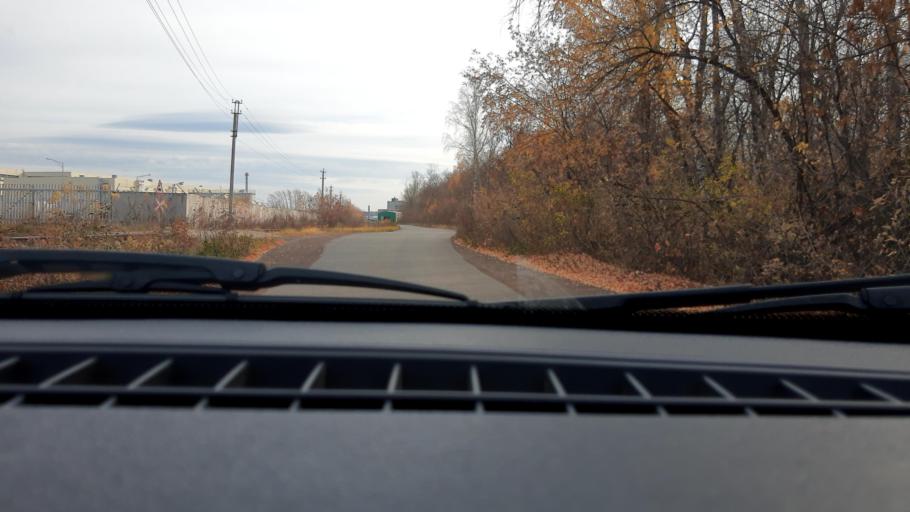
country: RU
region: Bashkortostan
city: Ufa
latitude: 54.5905
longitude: 55.9019
